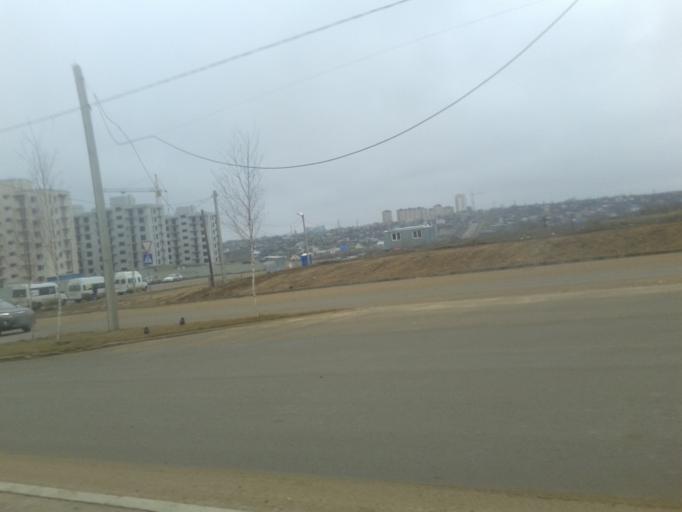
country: RU
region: Volgograd
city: Volgograd
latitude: 48.6618
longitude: 44.4149
